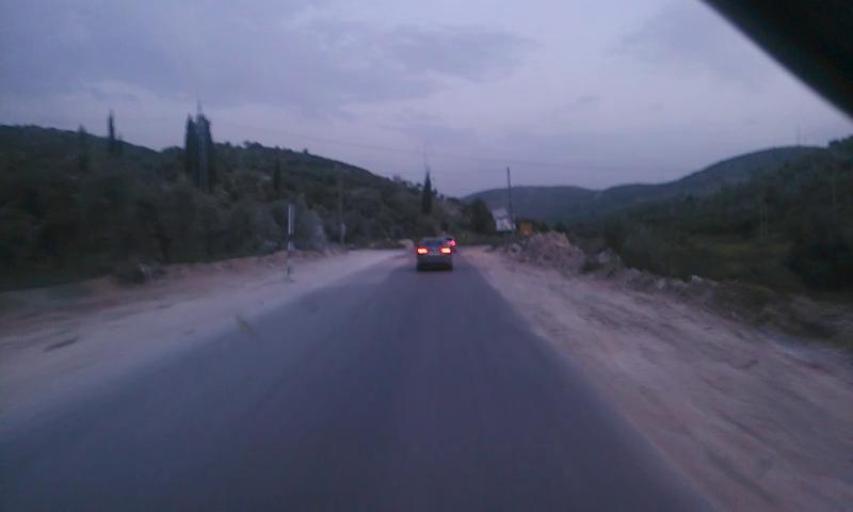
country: PS
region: West Bank
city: Ramin
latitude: 32.2955
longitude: 35.1329
